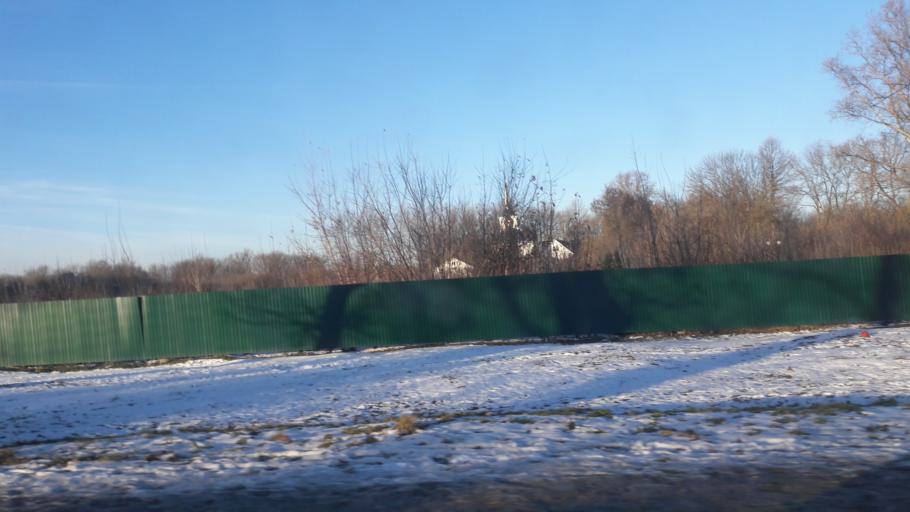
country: RU
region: Tula
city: Tula
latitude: 54.2088
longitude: 37.6451
